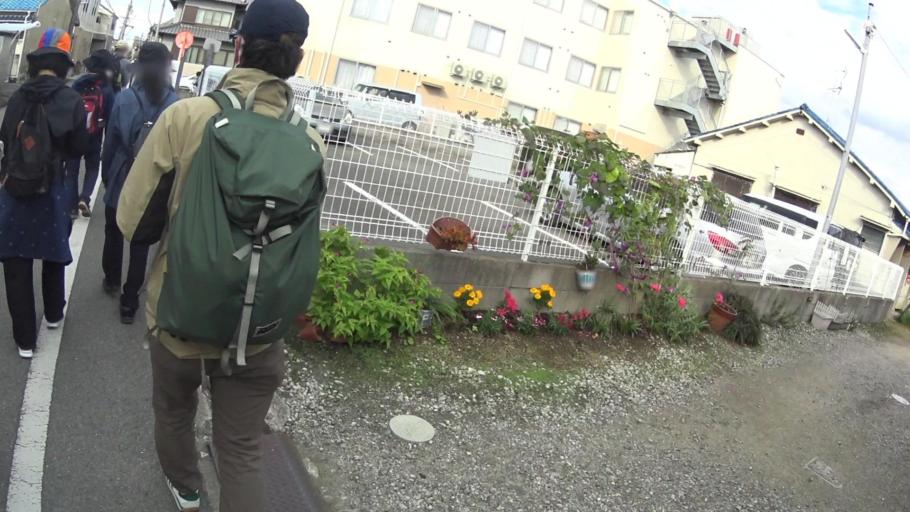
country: JP
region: Osaka
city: Kashihara
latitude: 34.5780
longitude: 135.5915
